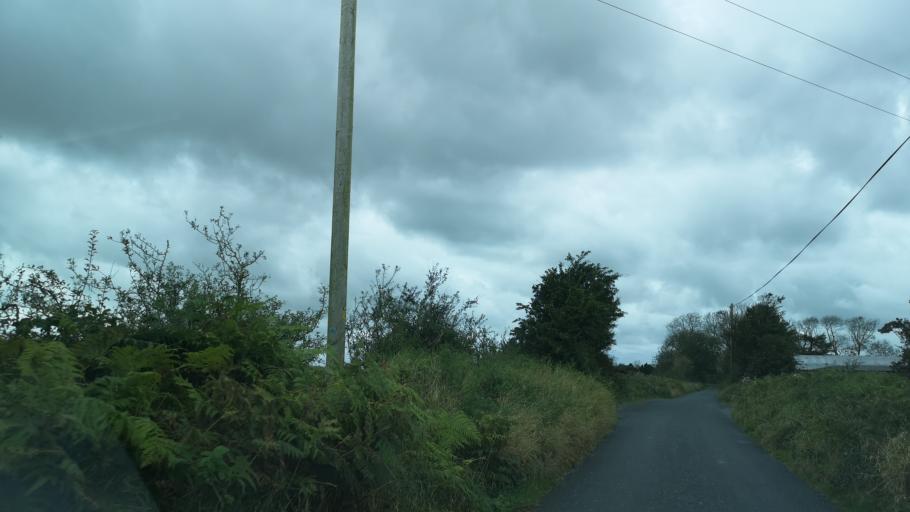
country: IE
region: Connaught
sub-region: County Galway
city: Athenry
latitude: 53.3240
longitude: -8.7386
